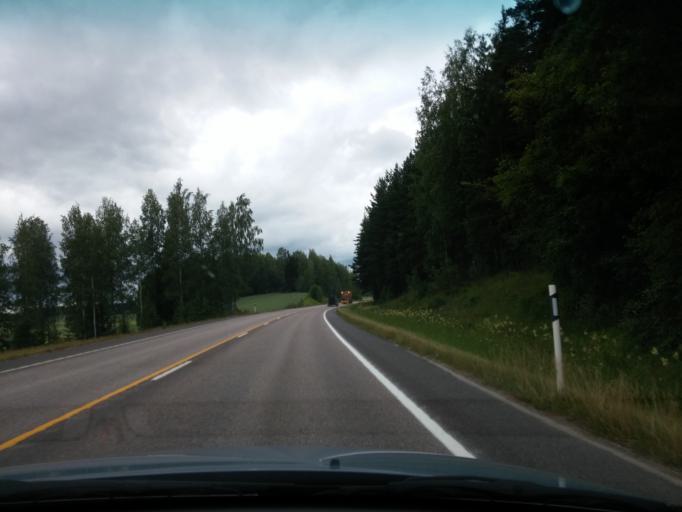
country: FI
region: Uusimaa
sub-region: Porvoo
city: Askola
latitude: 60.4699
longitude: 25.5701
